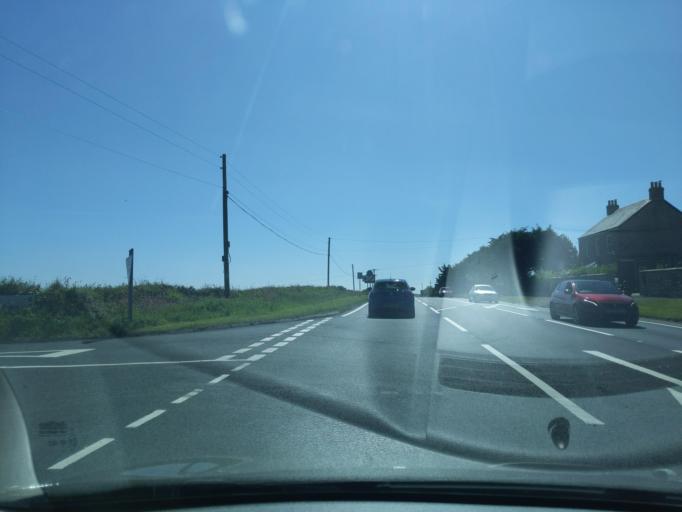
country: GB
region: England
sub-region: Cornwall
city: Wendron
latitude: 50.1526
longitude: -5.1951
